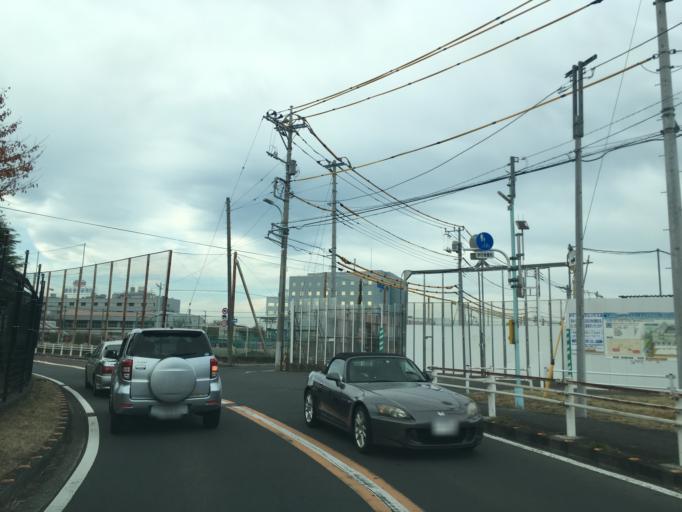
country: JP
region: Tokyo
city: Higashimurayama-shi
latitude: 35.7551
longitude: 139.4614
